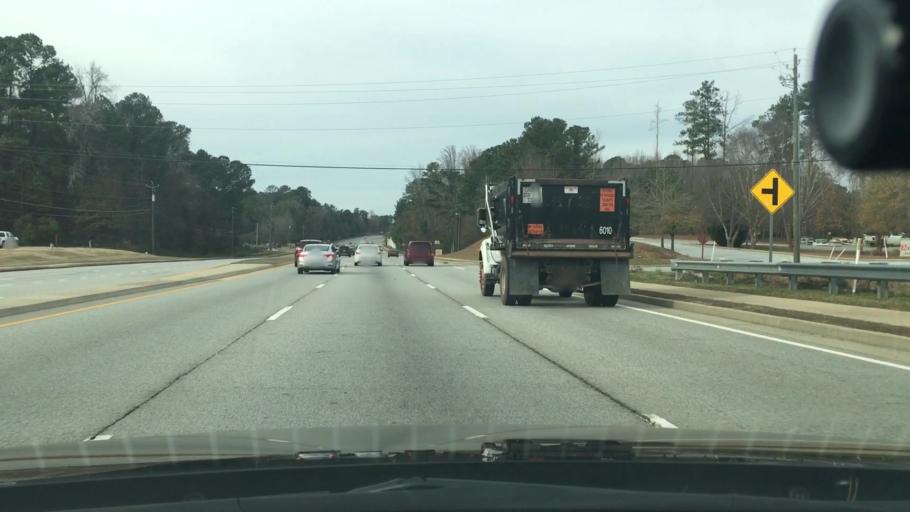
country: US
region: Georgia
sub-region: Fayette County
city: Peachtree City
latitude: 33.3748
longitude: -84.5716
